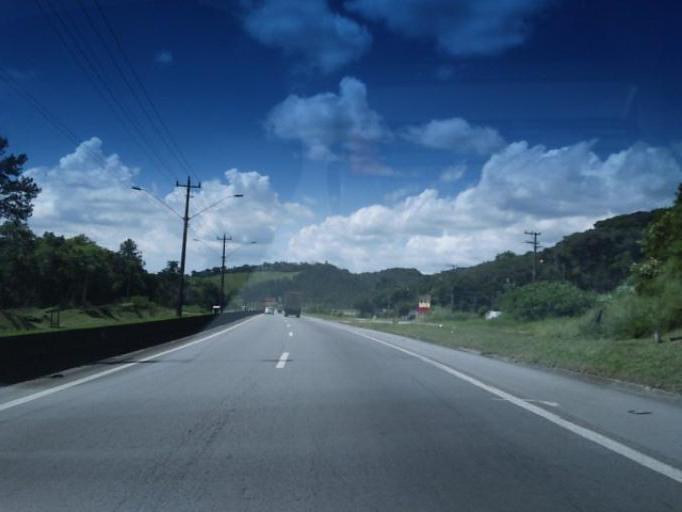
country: BR
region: Sao Paulo
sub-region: Sao Lourenco Da Serra
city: Sao Lourenco da Serra
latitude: -23.9052
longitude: -46.9918
